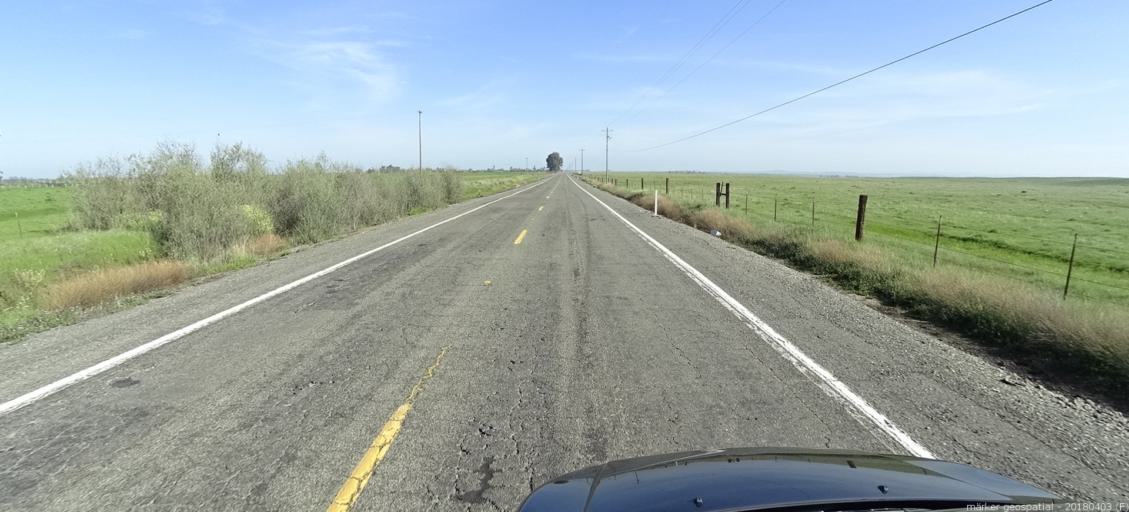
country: US
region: California
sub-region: Sacramento County
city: Clay
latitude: 38.3626
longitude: -121.1684
